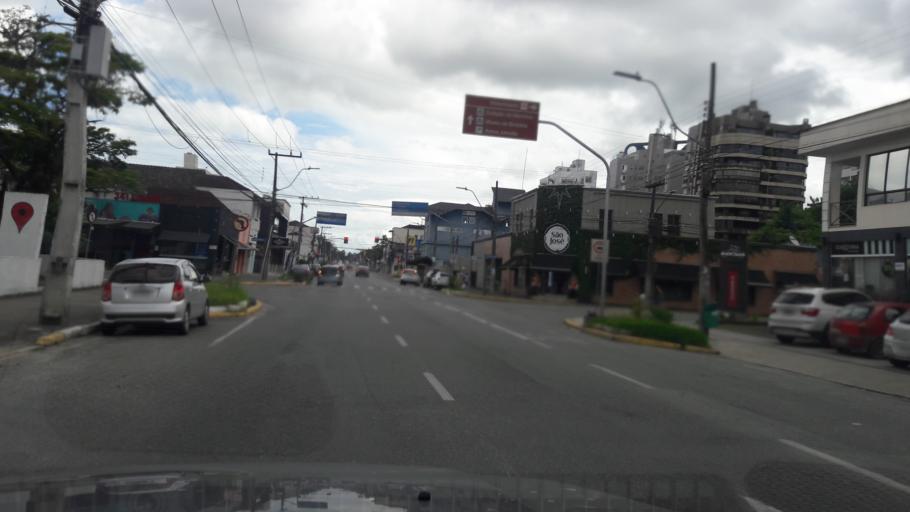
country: BR
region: Santa Catarina
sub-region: Joinville
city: Joinville
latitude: -26.3100
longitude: -48.8455
